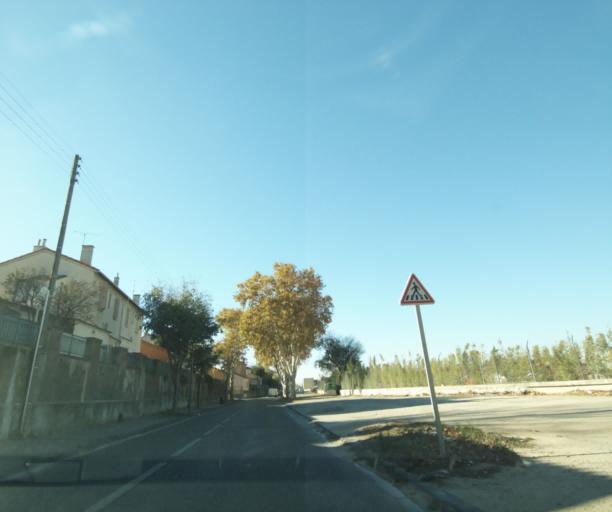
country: FR
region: Provence-Alpes-Cote d'Azur
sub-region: Departement des Bouches-du-Rhone
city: La Penne-sur-Huveaune
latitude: 43.2841
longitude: 5.4906
